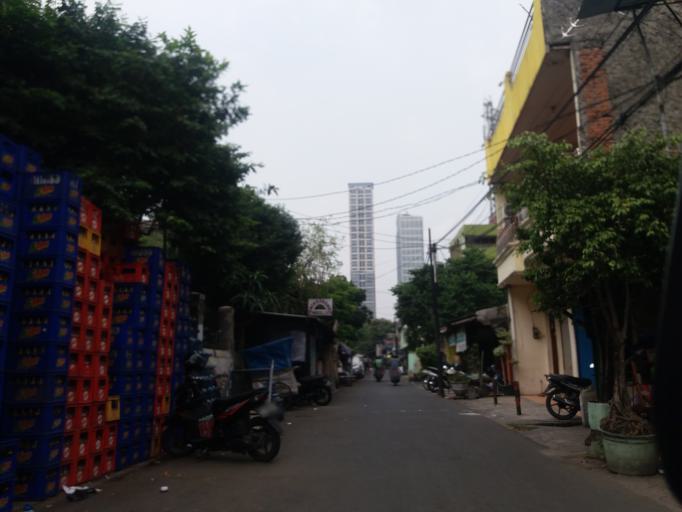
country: ID
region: Jakarta Raya
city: Jakarta
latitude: -6.1927
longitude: 106.8154
